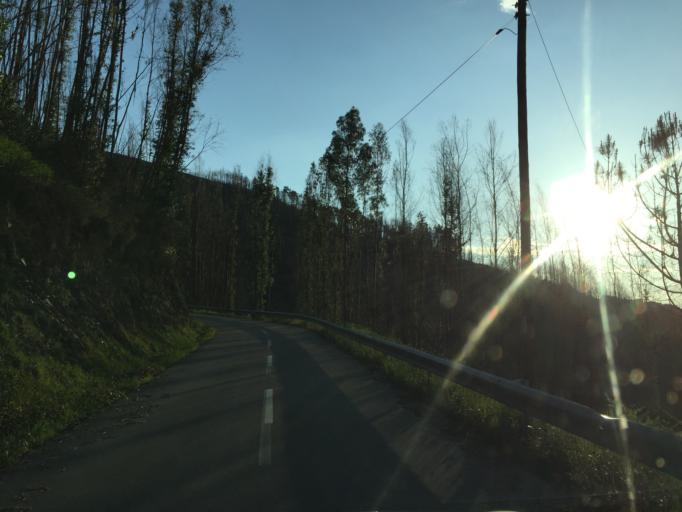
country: PT
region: Coimbra
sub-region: Arganil
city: Arganil
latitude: 40.1300
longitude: -8.0080
